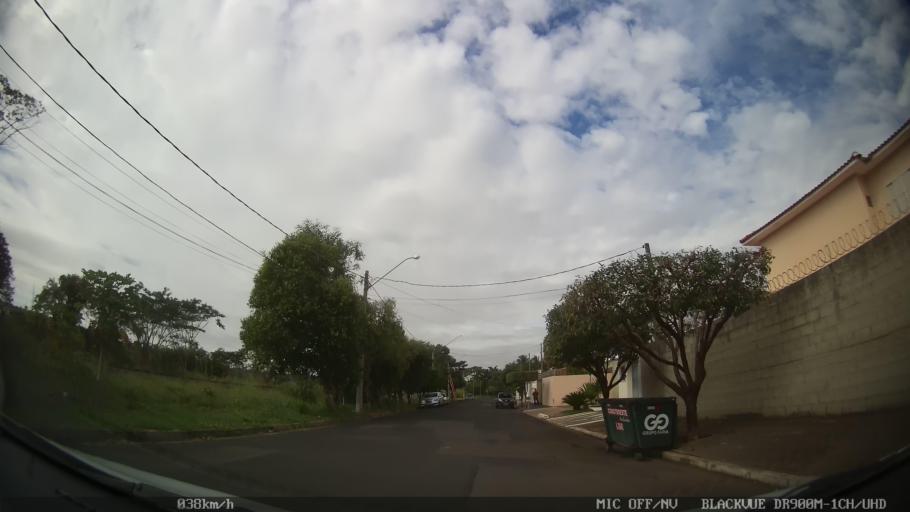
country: BR
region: Sao Paulo
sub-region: Sao Jose Do Rio Preto
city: Sao Jose do Rio Preto
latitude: -20.8191
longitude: -49.3495
